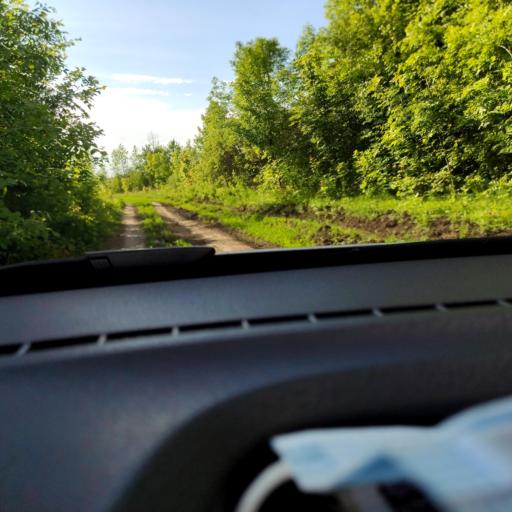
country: RU
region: Voronezj
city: Ramon'
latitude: 51.9483
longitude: 39.3612
